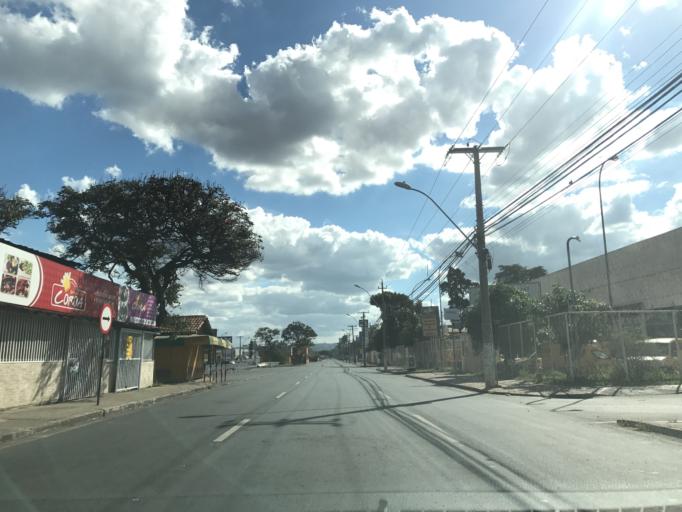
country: BR
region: Federal District
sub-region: Brasilia
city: Brasilia
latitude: -15.8042
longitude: -47.9569
